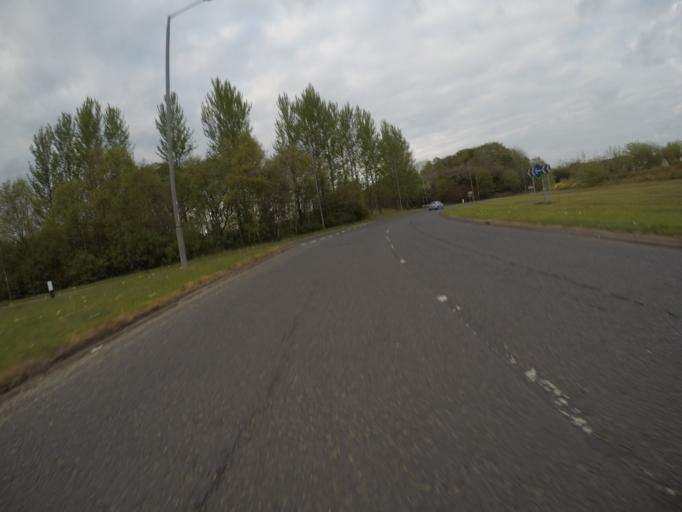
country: GB
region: Scotland
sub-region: North Ayrshire
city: Irvine
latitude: 55.6330
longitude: -4.6472
